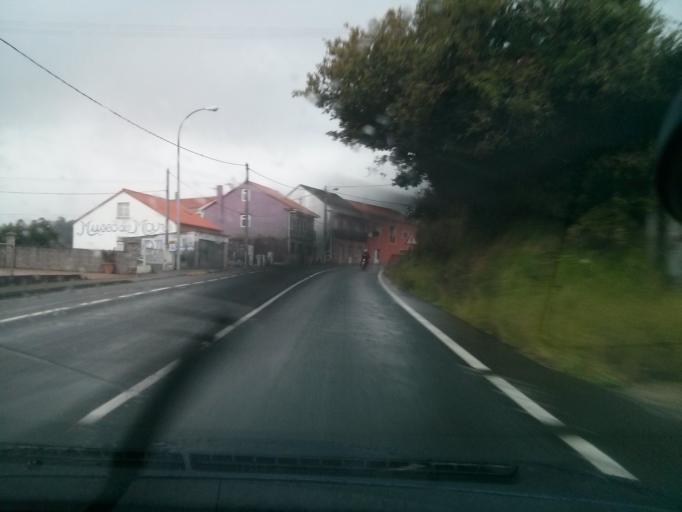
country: ES
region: Galicia
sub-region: Provincia da Coruna
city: Noia
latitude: 42.8071
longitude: -8.8858
